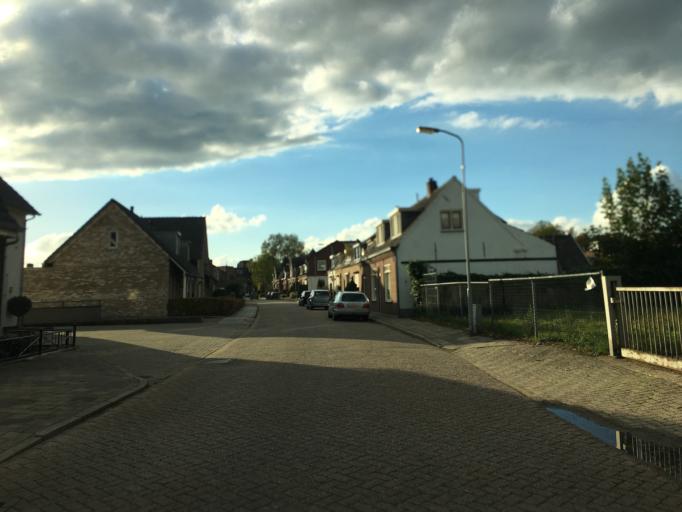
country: NL
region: Gelderland
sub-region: Gemeente Montferland
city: s-Heerenberg
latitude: 51.8768
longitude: 6.2512
